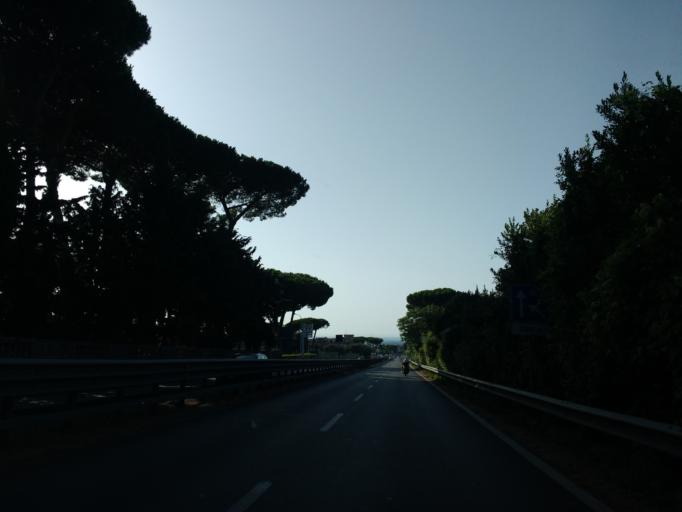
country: IT
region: Latium
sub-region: Citta metropolitana di Roma Capitale
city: Marino
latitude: 41.7571
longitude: 12.6272
